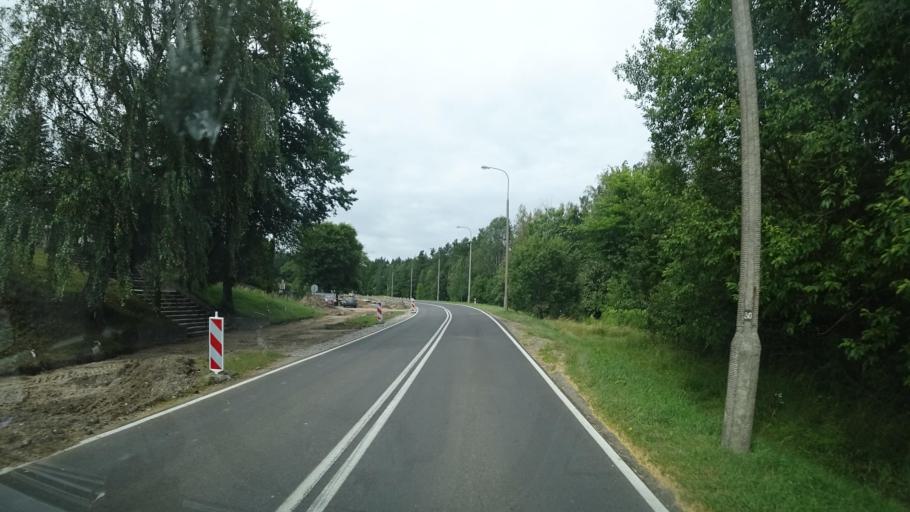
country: PL
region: Warmian-Masurian Voivodeship
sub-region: Powiat goldapski
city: Goldap
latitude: 54.3230
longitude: 22.2983
